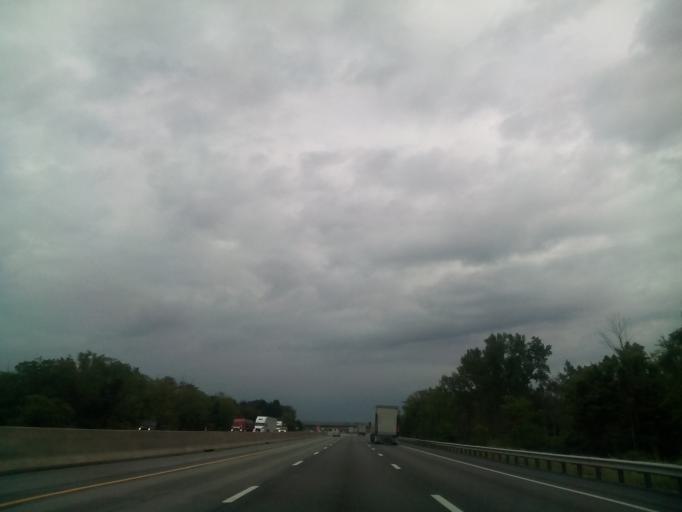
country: US
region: Ohio
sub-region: Ottawa County
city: Elmore
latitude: 41.4682
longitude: -83.3117
